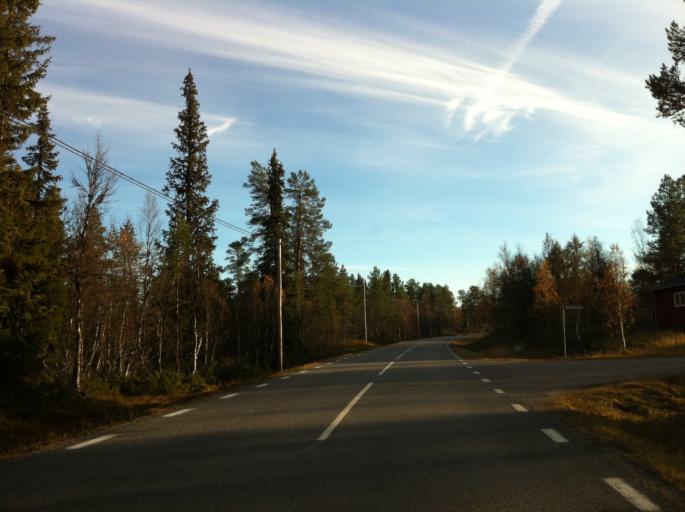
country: NO
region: Hedmark
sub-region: Engerdal
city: Engerdal
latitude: 62.0669
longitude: 12.2209
